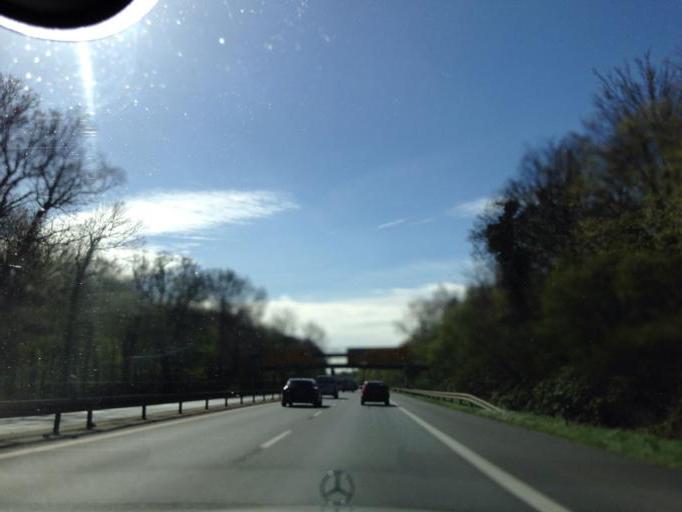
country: DE
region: Lower Saxony
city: Laatzen
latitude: 52.3421
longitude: 9.8011
